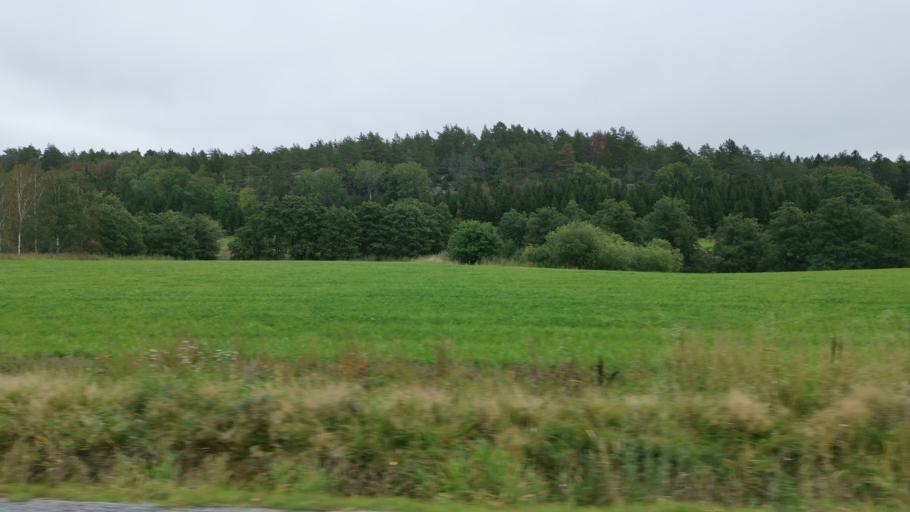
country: SE
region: Vaestra Goetaland
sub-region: Tanums Kommun
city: Tanumshede
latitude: 58.6307
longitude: 11.3476
